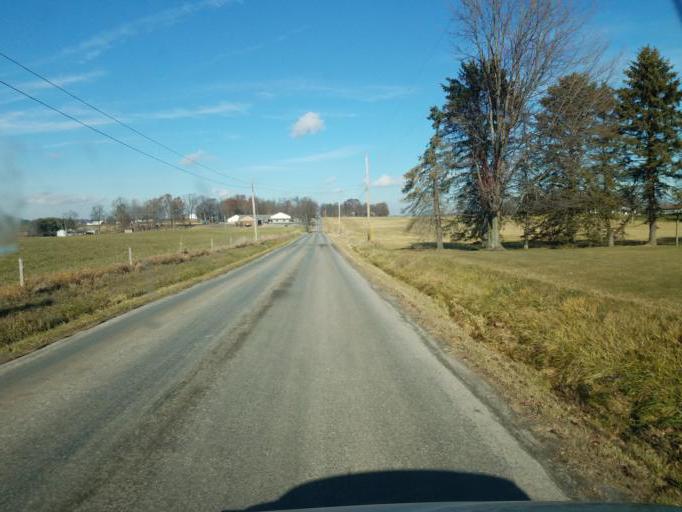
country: US
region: Ohio
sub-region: Wayne County
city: Apple Creek
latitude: 40.7413
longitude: -81.7752
